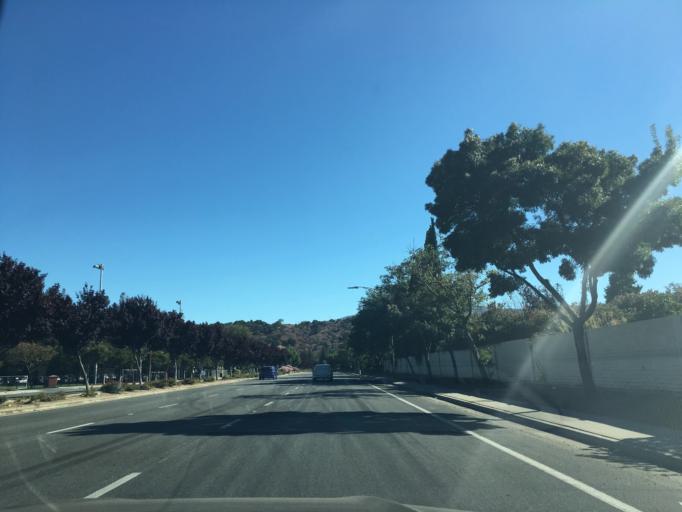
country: US
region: California
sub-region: Santa Clara County
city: Seven Trees
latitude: 37.2474
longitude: -121.8596
